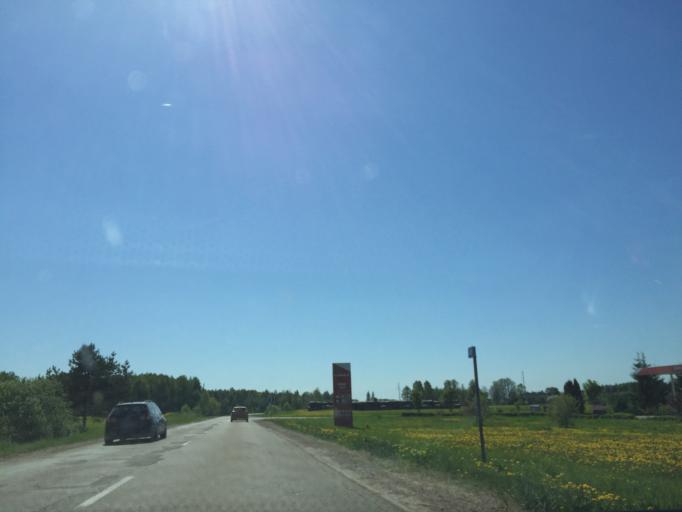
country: LV
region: Malpils
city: Malpils
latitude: 56.9296
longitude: 24.9351
